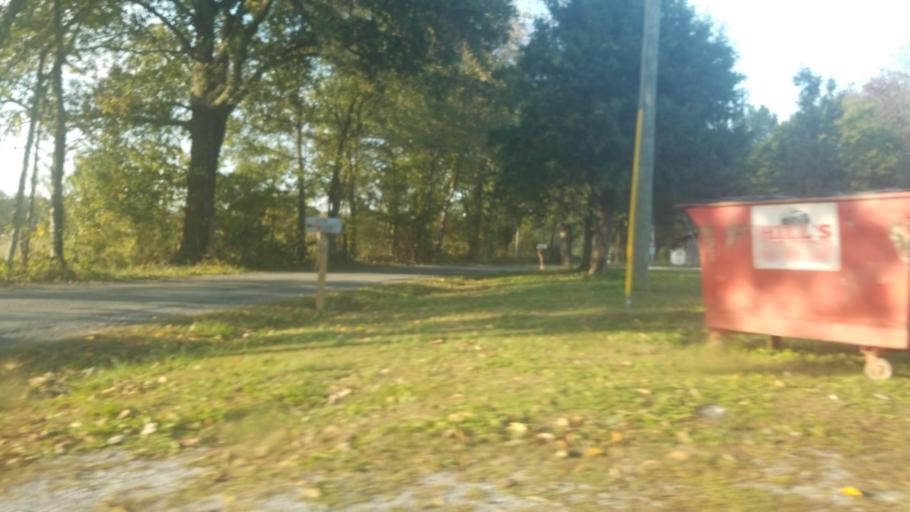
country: US
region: Illinois
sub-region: Williamson County
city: Marion
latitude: 37.7667
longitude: -88.8080
